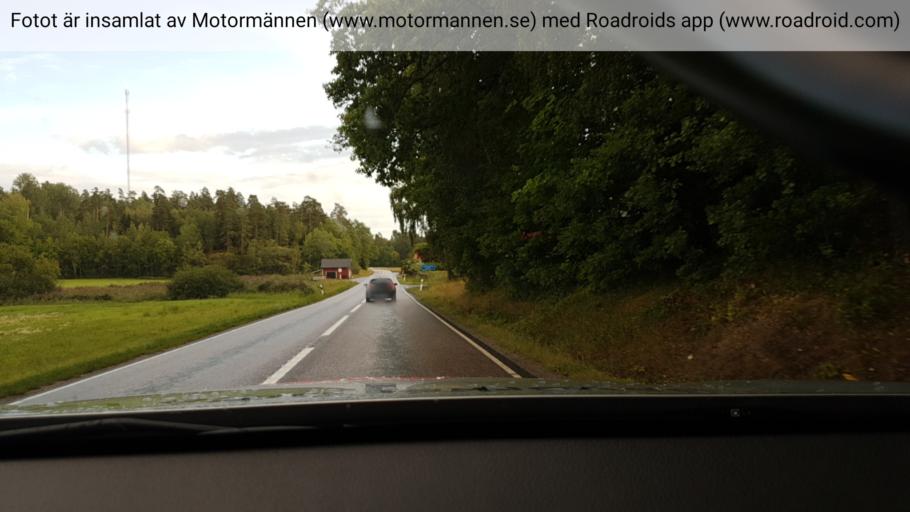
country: SE
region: Stockholm
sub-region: Norrtalje Kommun
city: Norrtalje
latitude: 59.8074
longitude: 18.6498
